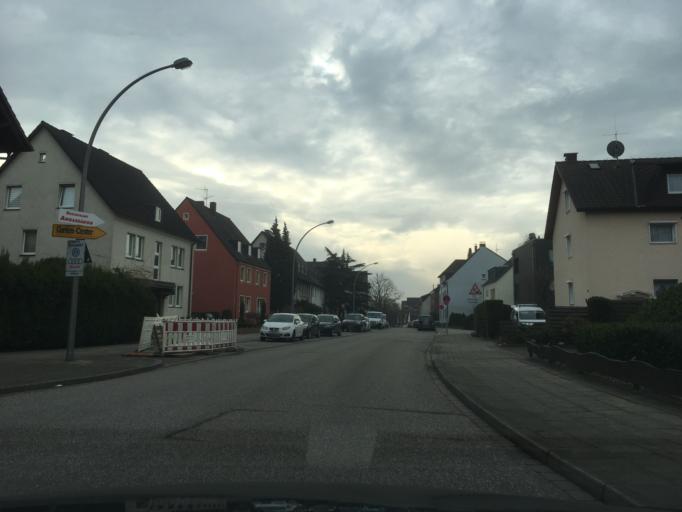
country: DE
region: North Rhine-Westphalia
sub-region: Regierungsbezirk Munster
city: Gladbeck
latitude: 51.5782
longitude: 6.9939
